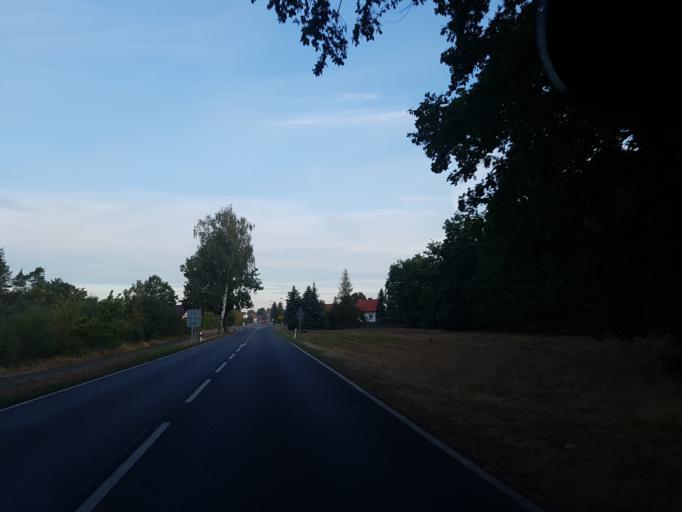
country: DE
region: Brandenburg
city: Sonnewalde
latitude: 51.6626
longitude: 13.6501
